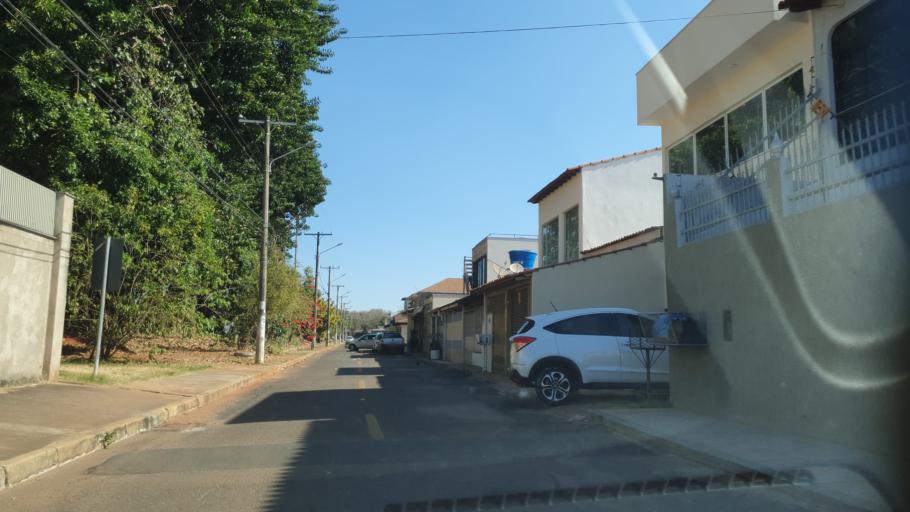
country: BR
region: Federal District
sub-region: Brasilia
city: Brasilia
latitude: -15.7822
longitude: -47.9323
